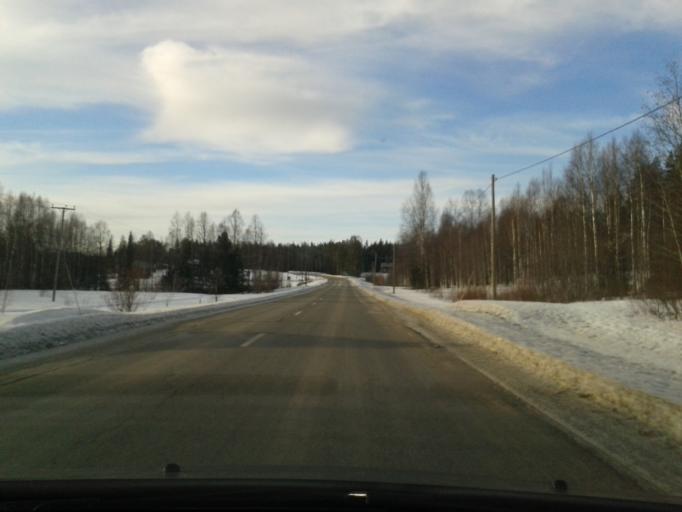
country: SE
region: Vaesternorrland
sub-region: OErnskoeldsviks Kommun
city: Bredbyn
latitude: 63.5290
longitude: 17.9887
